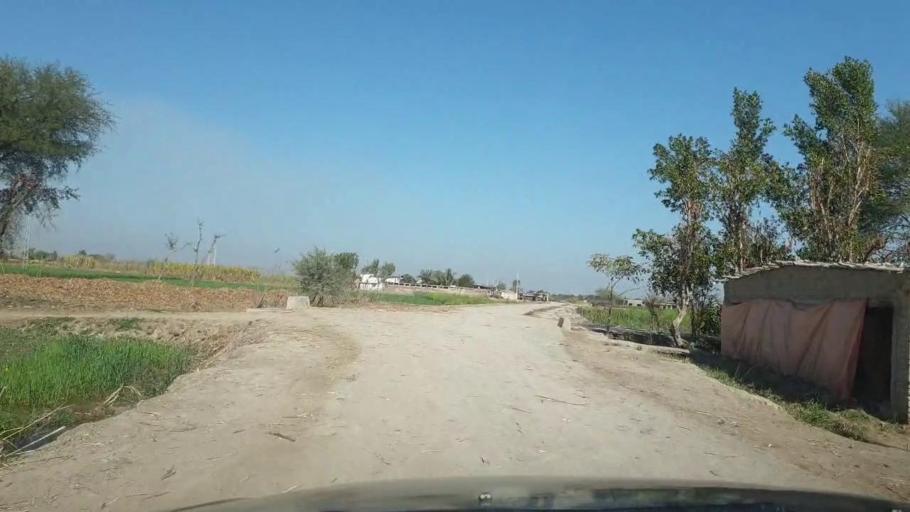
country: PK
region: Sindh
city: Mirpur Khas
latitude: 25.5648
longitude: 69.0566
